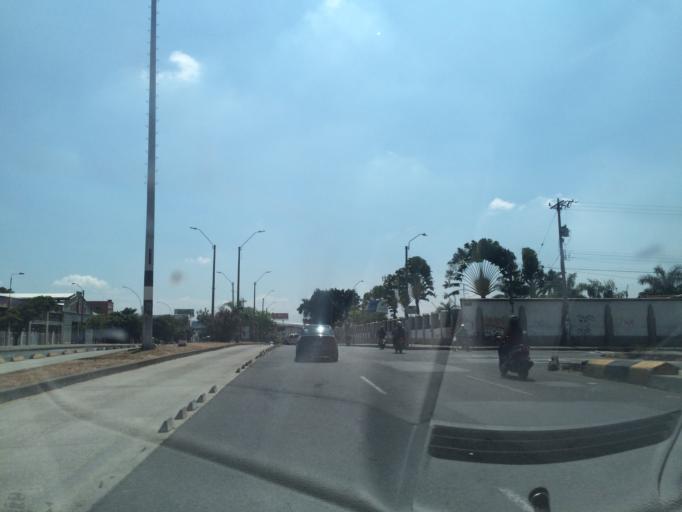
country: CO
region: Valle del Cauca
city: Cali
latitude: 3.4613
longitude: -76.5199
